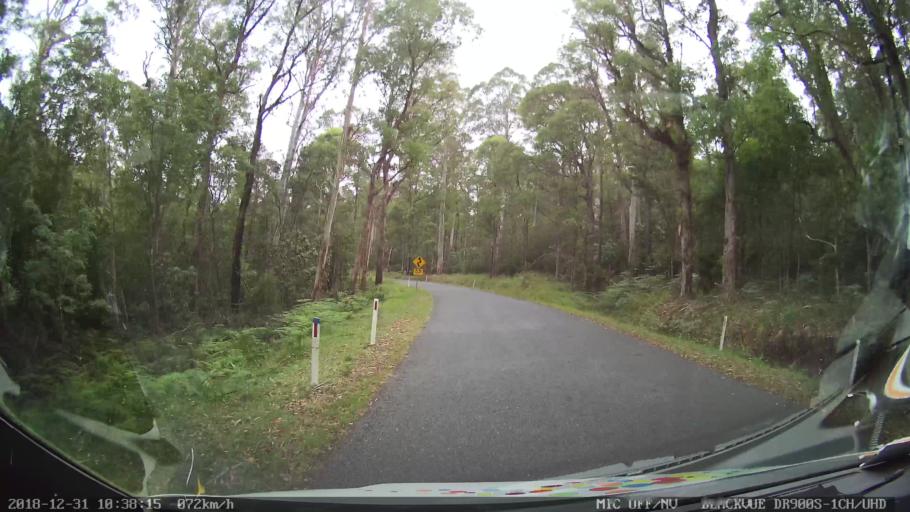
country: AU
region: New South Wales
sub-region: Snowy River
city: Jindabyne
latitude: -36.4091
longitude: 148.1776
